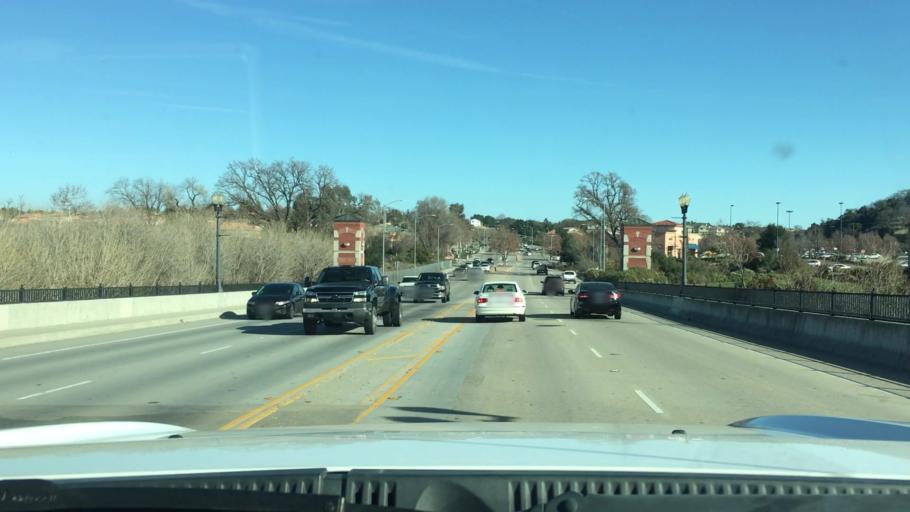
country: US
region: California
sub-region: San Luis Obispo County
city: Paso Robles
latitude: 35.6151
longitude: -120.6859
